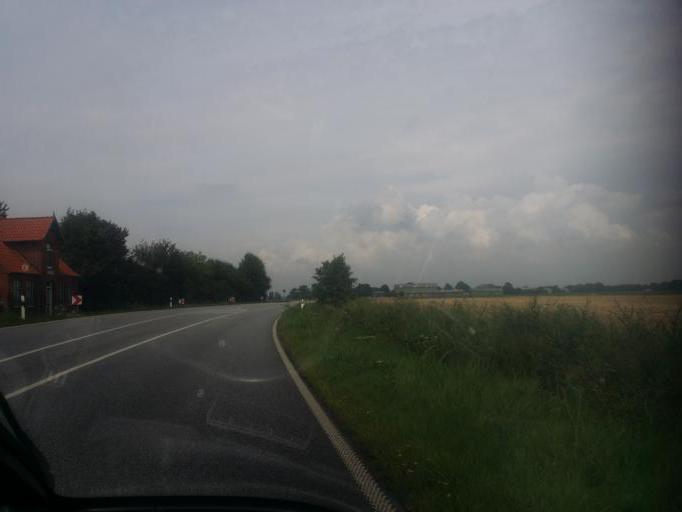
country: DE
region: Schleswig-Holstein
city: Meldorf
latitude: 54.1028
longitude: 9.0585
